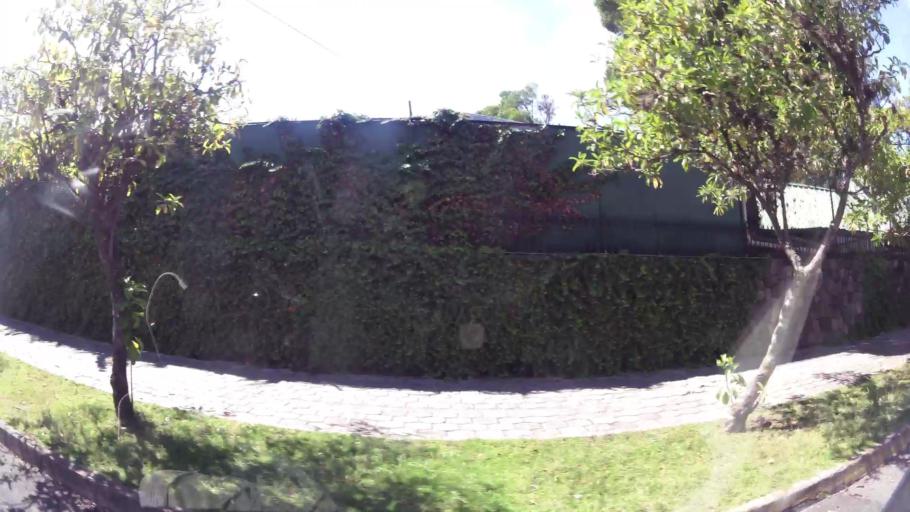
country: EC
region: Pichincha
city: Quito
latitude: -0.1964
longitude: -78.4365
